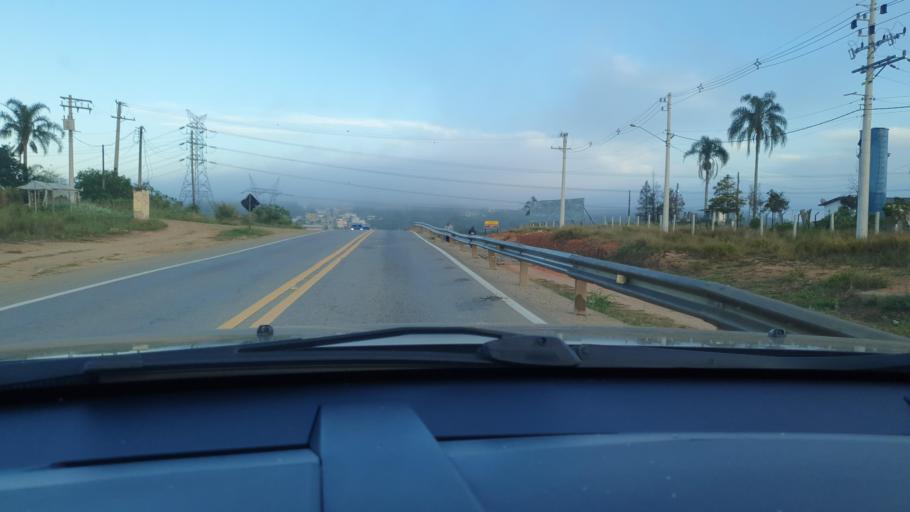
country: BR
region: Sao Paulo
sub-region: Vargem Grande Paulista
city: Vargem Grande Paulista
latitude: -23.6571
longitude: -47.0795
